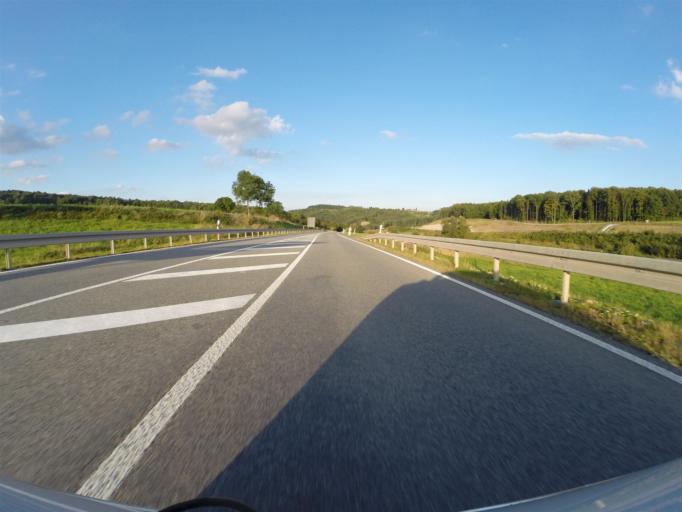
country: DE
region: Thuringia
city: Bucha
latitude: 50.8786
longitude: 11.5236
